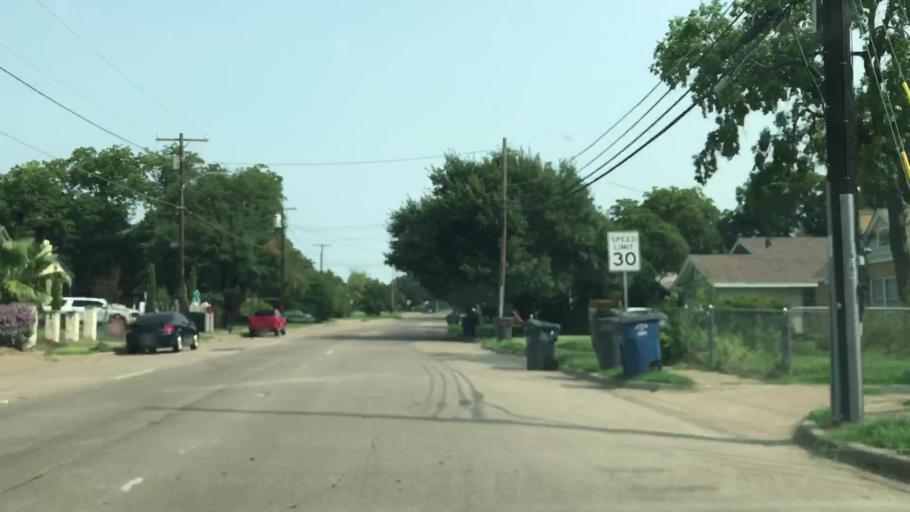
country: US
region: Texas
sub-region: Dallas County
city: Dallas
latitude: 32.7503
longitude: -96.8376
